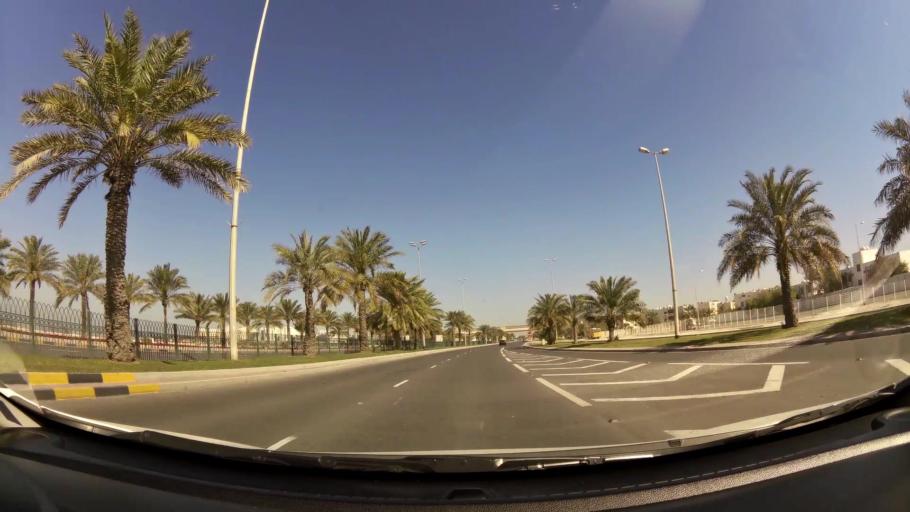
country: BH
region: Muharraq
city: Al Muharraq
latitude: 26.2550
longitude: 50.6034
